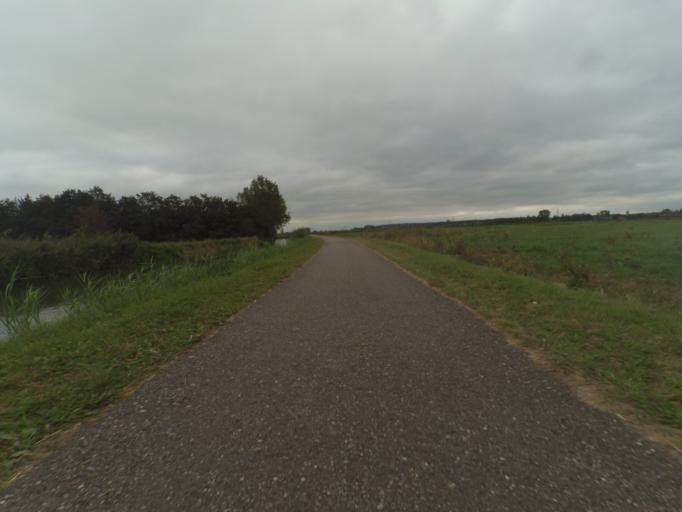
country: NL
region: Utrecht
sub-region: Gemeente Rhenen
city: Rhenen
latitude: 51.9875
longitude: 5.6141
